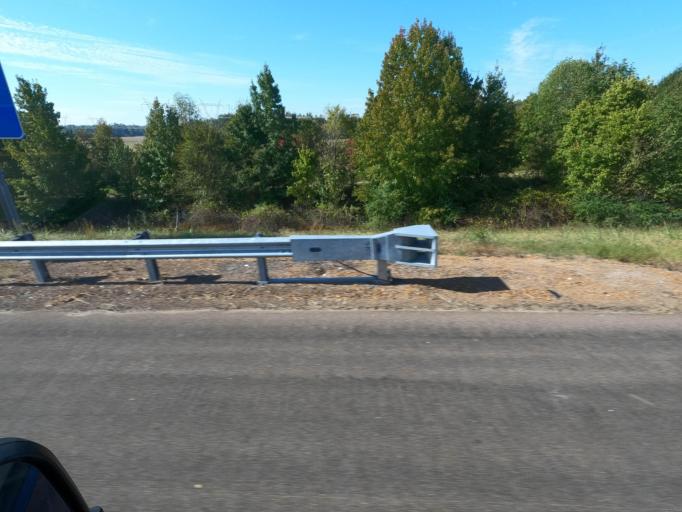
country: US
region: Tennessee
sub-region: Shelby County
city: Arlington
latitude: 35.3048
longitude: -89.6980
